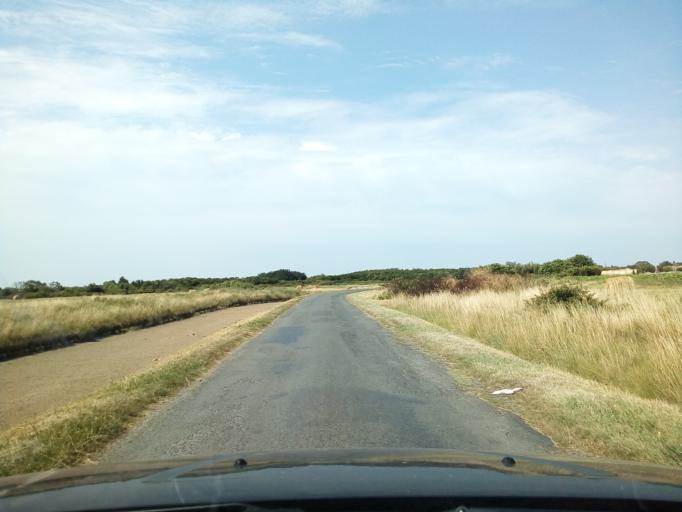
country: FR
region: Poitou-Charentes
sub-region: Departement de la Charente-Maritime
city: Dolus-d'Oleron
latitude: 45.9481
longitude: -1.2882
